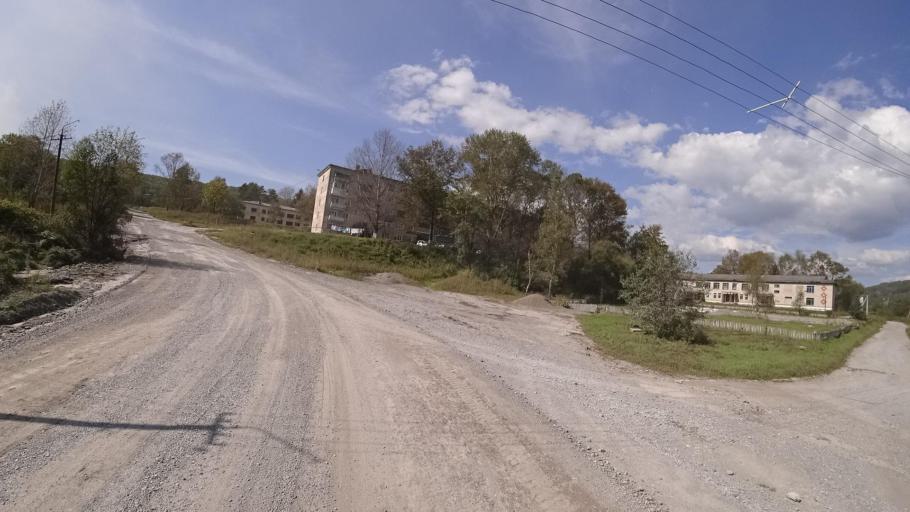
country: RU
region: Jewish Autonomous Oblast
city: Londoko
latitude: 49.0236
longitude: 131.9262
